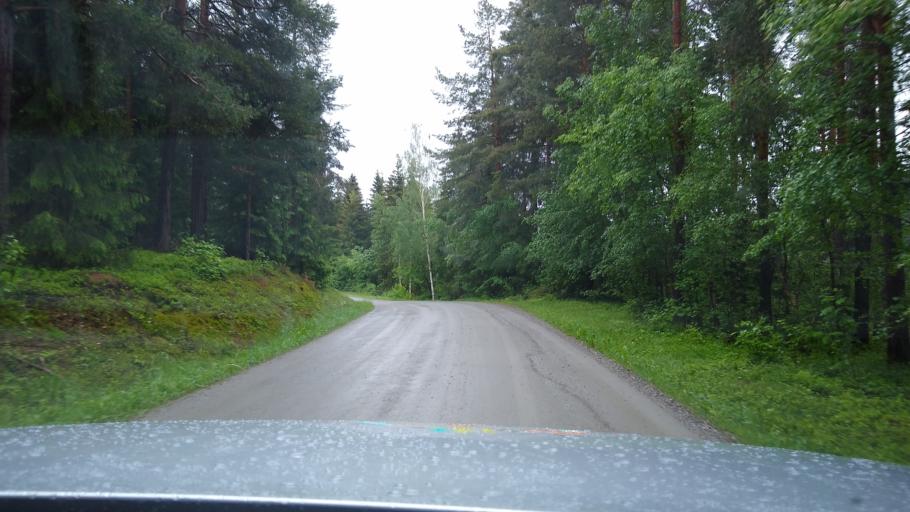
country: NO
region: Oppland
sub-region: Ringebu
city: Ringebu
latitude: 61.5433
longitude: 10.1032
